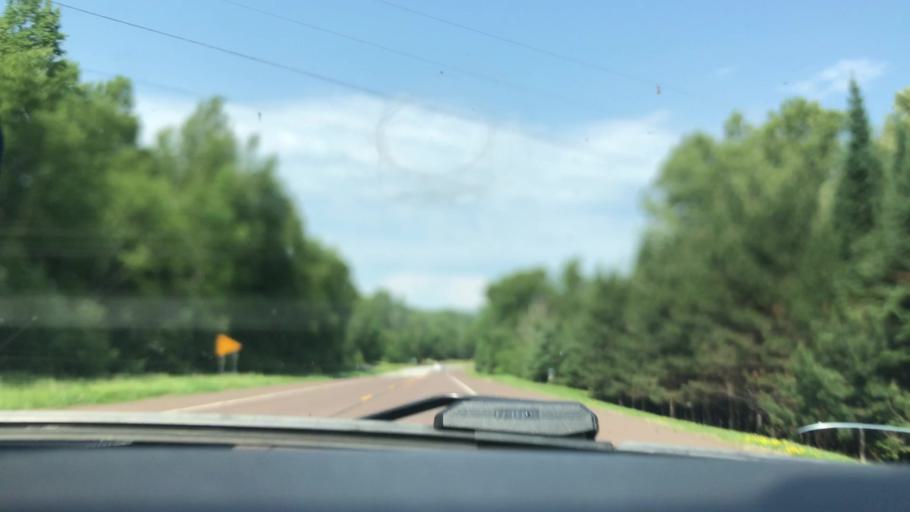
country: US
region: Minnesota
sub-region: Cook County
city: Grand Marais
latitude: 47.7816
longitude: -90.1868
